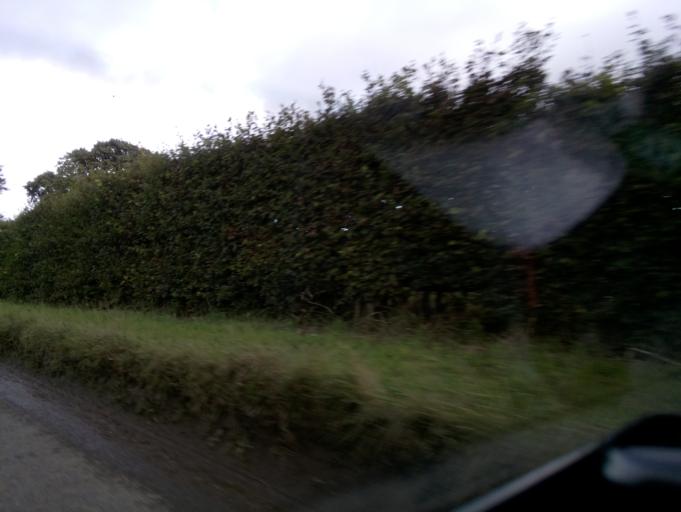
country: GB
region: England
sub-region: Devon
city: Kingsbridge
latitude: 50.2988
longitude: -3.7929
